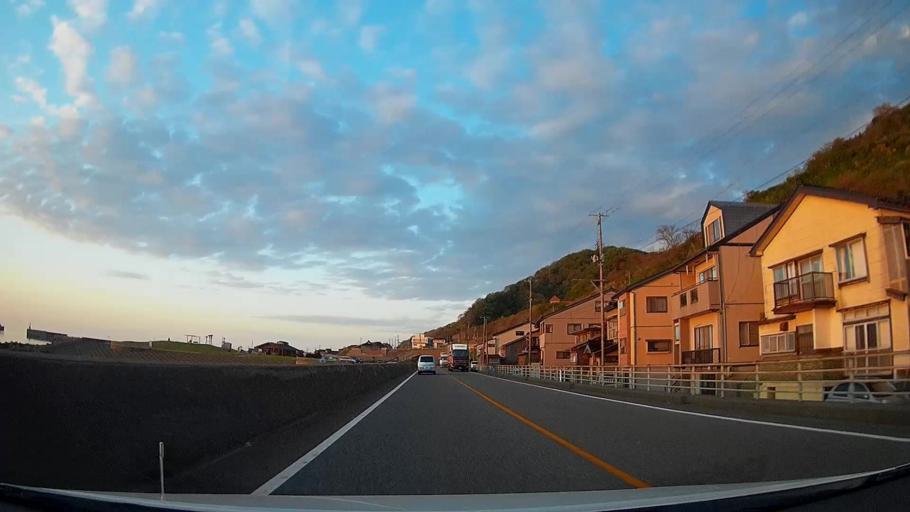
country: JP
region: Niigata
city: Joetsu
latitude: 37.1299
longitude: 138.0511
